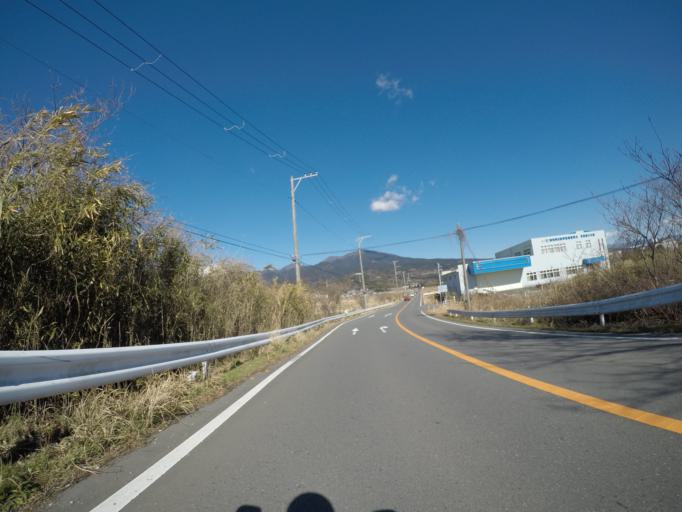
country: JP
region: Shizuoka
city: Numazu
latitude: 35.1354
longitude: 138.7820
